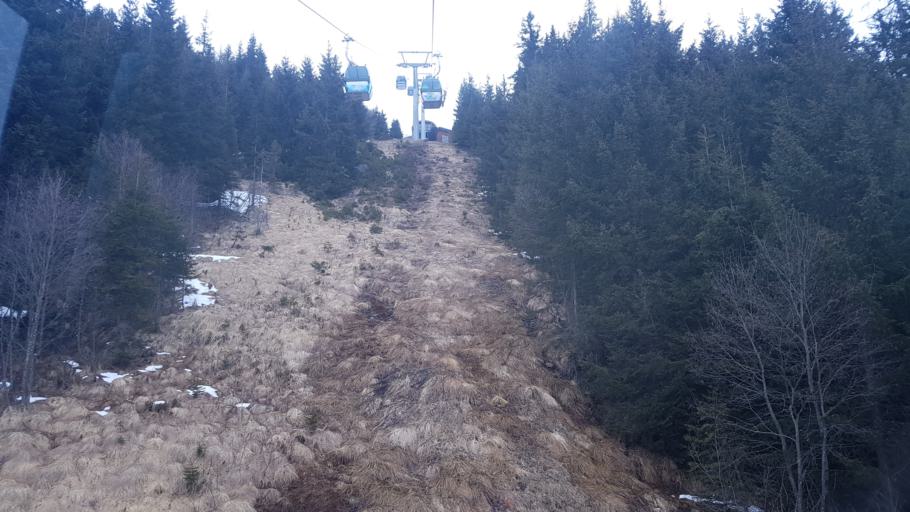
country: AT
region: Salzburg
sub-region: Politischer Bezirk Zell am See
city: Neukirchen am Grossvenediger
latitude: 47.2685
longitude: 12.2809
